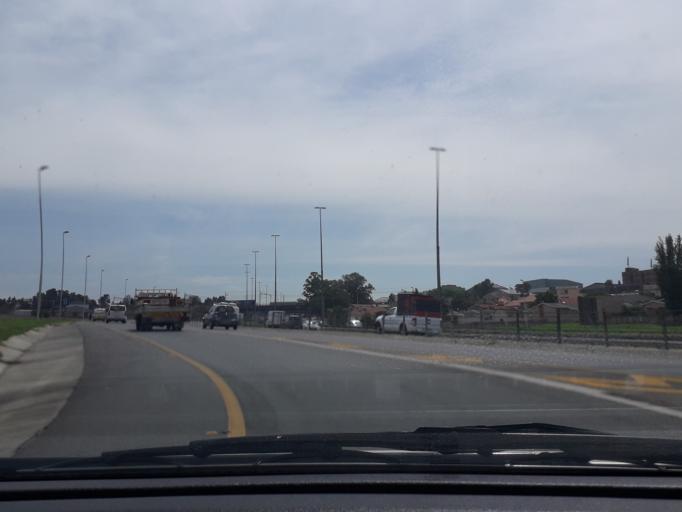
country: ZA
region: Gauteng
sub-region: City of Johannesburg Metropolitan Municipality
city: Roodepoort
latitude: -26.1852
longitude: 27.9455
